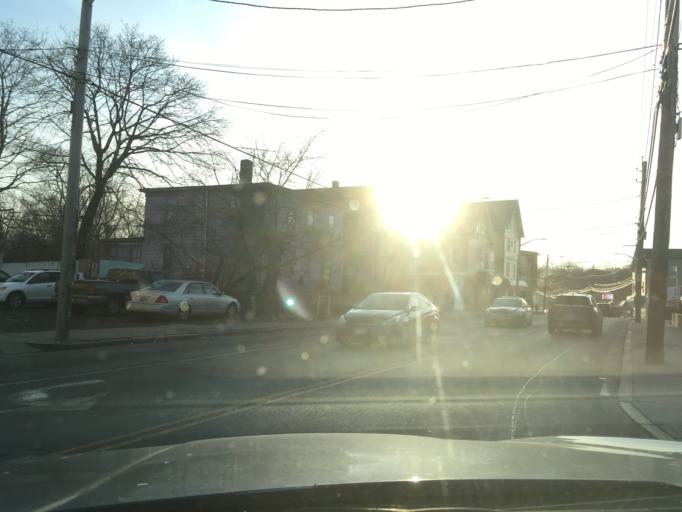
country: US
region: Rhode Island
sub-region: Providence County
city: North Providence
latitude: 41.8340
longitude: -71.4680
